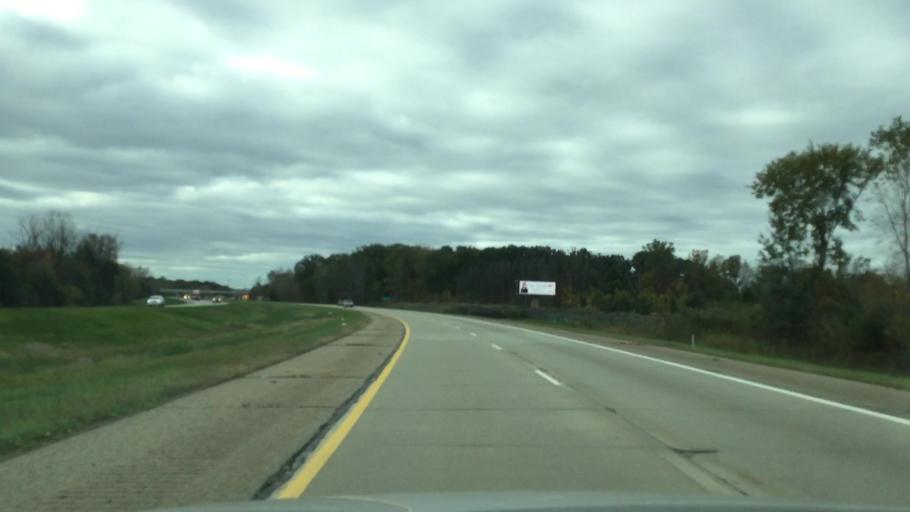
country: US
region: Michigan
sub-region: Macomb County
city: Romeo
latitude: 42.7521
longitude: -83.0193
